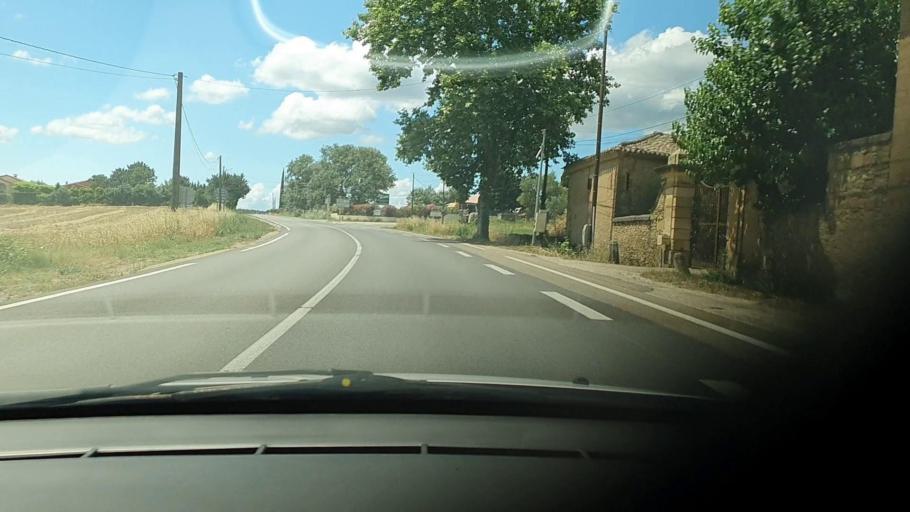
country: FR
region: Languedoc-Roussillon
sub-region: Departement du Gard
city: Montaren-et-Saint-Mediers
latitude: 44.0393
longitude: 4.3517
